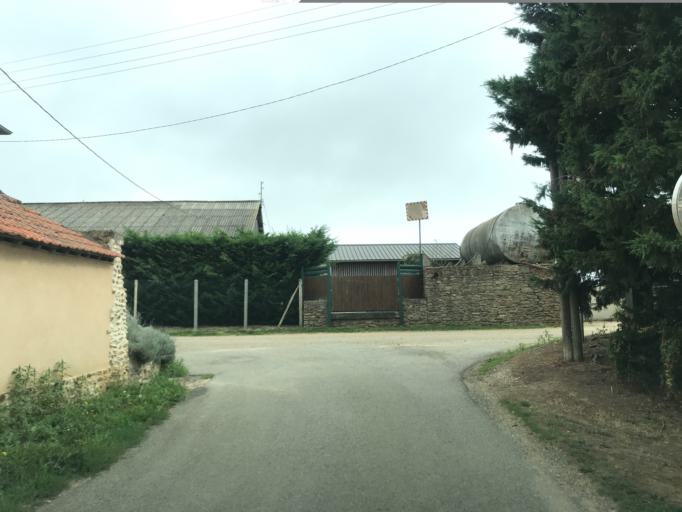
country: FR
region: Haute-Normandie
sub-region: Departement de l'Eure
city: Houlbec-Cocherel
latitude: 49.0534
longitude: 1.3533
